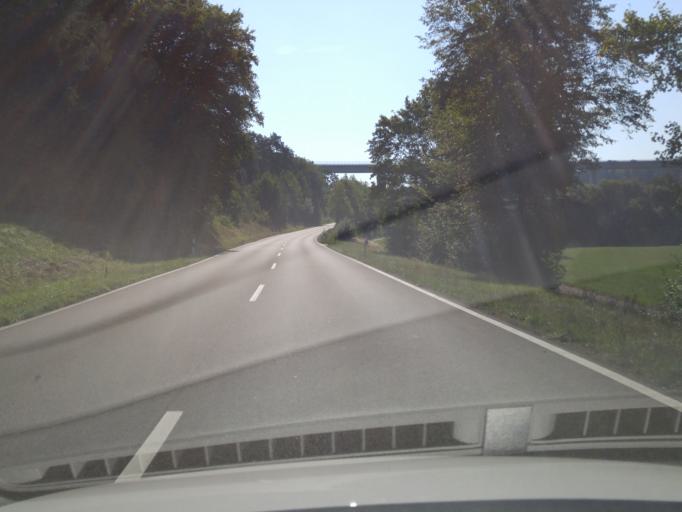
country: DE
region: Baden-Wuerttemberg
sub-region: Regierungsbezirk Stuttgart
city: Schlaitdorf
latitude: 48.6227
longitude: 9.2197
